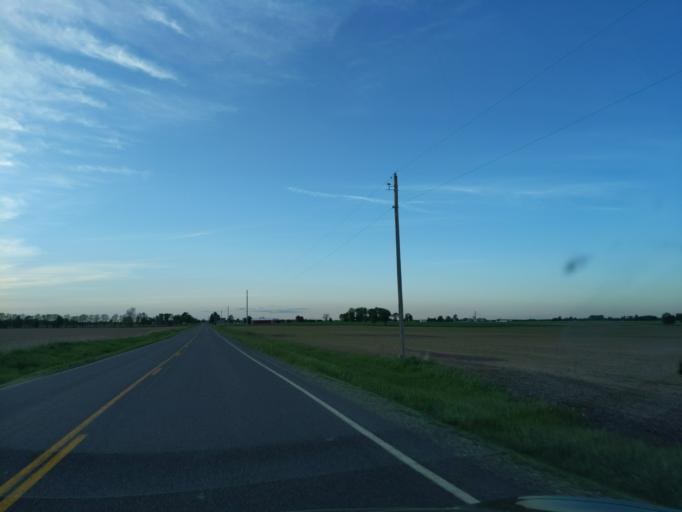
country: US
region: Michigan
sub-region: Ingham County
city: Williamston
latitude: 42.5868
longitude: -84.2986
